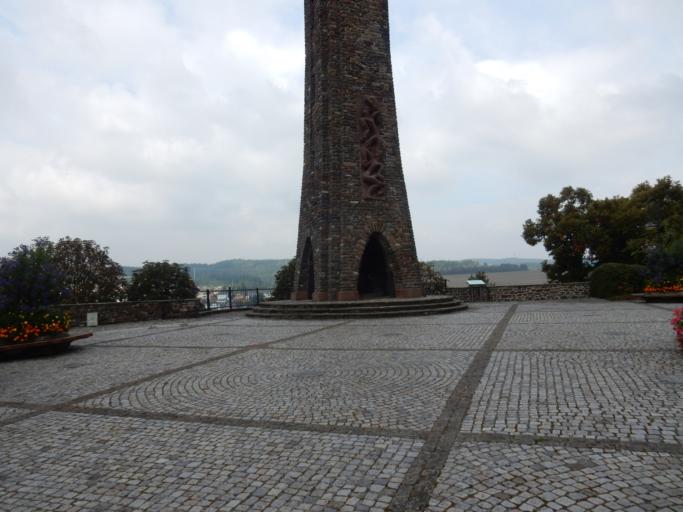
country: LU
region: Diekirch
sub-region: Canton de Wiltz
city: Wiltz
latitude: 49.9663
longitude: 5.9340
